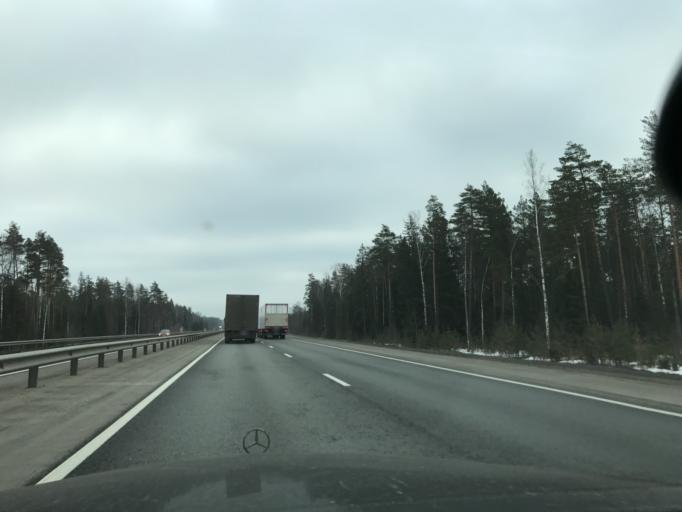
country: RU
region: Vladimir
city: Sudogda
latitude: 56.1067
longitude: 40.7992
